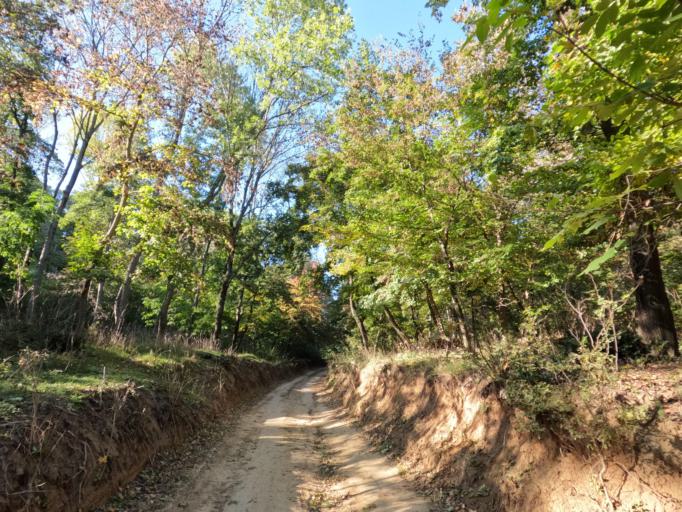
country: HU
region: Tolna
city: Szentgalpuszta
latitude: 46.3219
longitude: 18.6554
